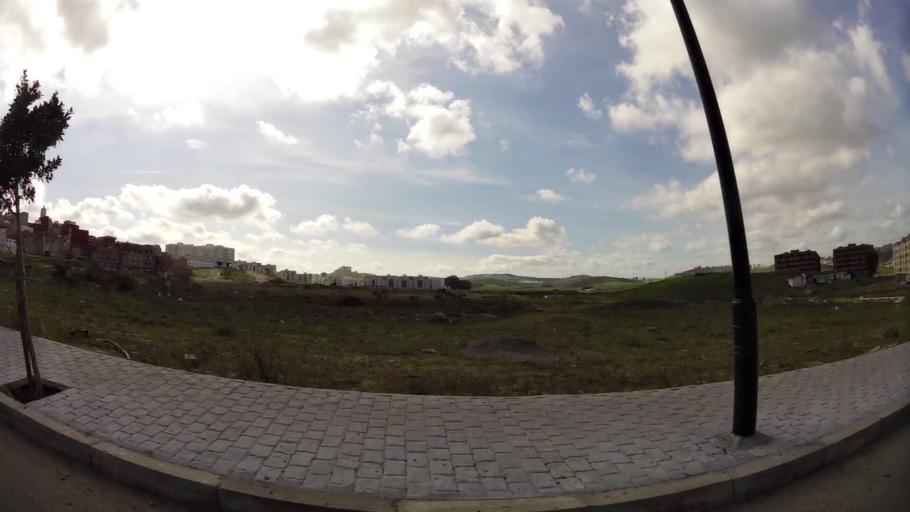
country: MA
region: Tanger-Tetouan
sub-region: Tanger-Assilah
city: Tangier
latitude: 35.7650
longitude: -5.7682
